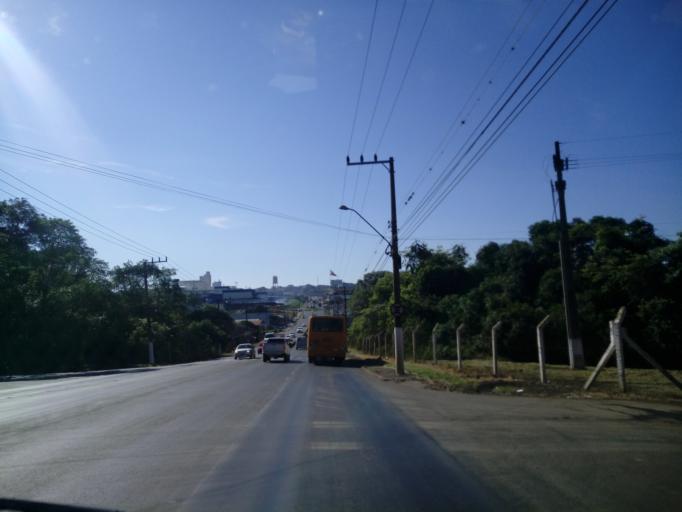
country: BR
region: Santa Catarina
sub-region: Chapeco
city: Chapeco
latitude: -27.0972
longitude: -52.6584
